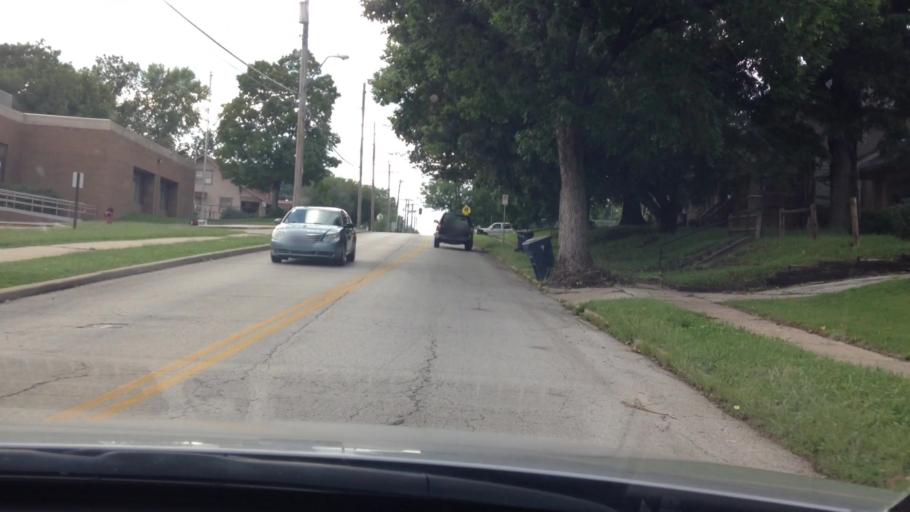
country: US
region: Kansas
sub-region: Johnson County
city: Mission Hills
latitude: 39.0199
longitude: -94.5719
